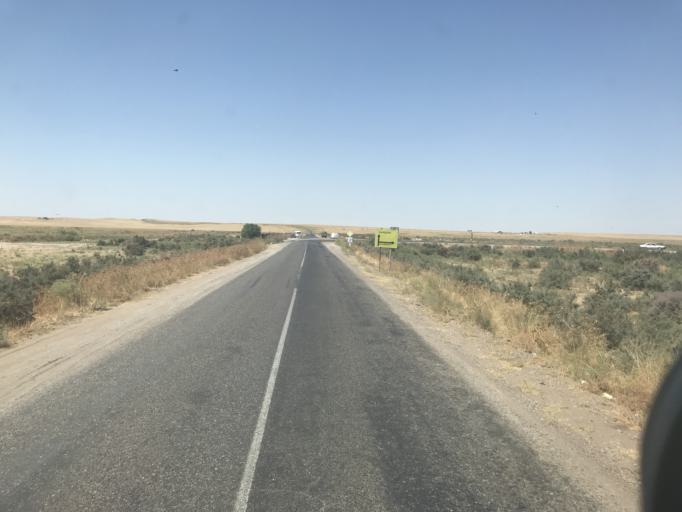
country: UZ
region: Toshkent
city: Chinoz
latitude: 41.2040
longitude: 68.5876
